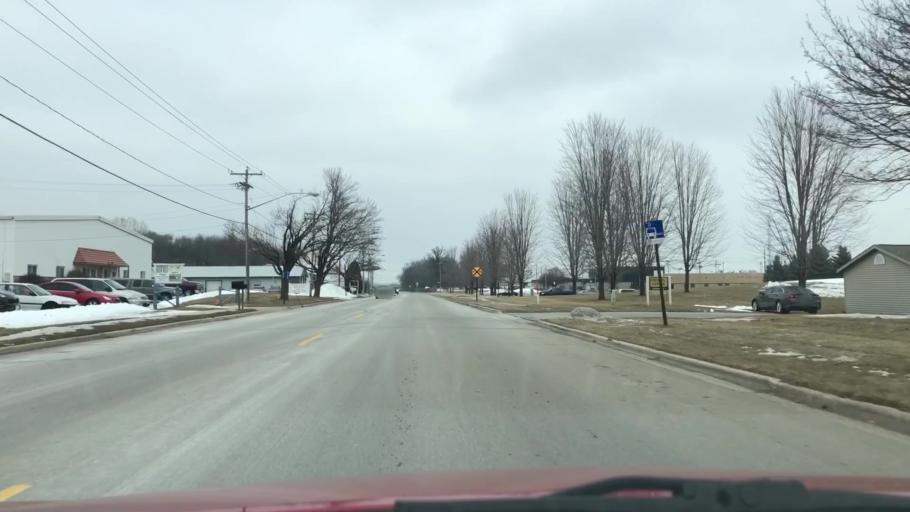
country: US
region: Wisconsin
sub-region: Brown County
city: Ashwaubenon
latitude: 44.4664
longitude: -88.0756
